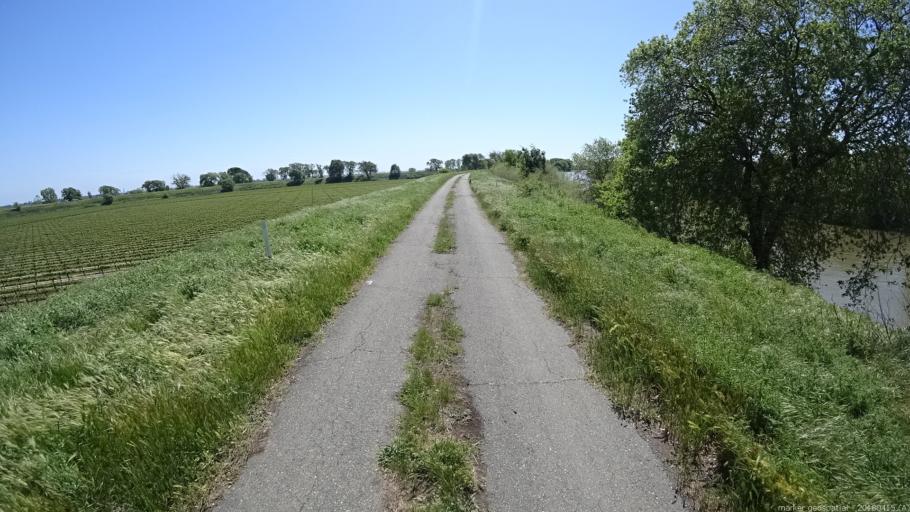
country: US
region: California
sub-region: Sacramento County
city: Walnut Grove
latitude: 38.2579
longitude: -121.5998
